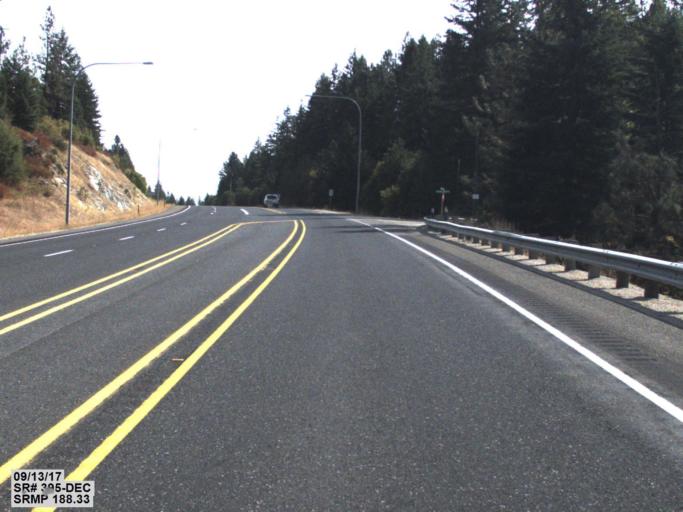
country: US
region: Washington
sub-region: Spokane County
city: Deer Park
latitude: 48.0307
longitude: -117.6019
